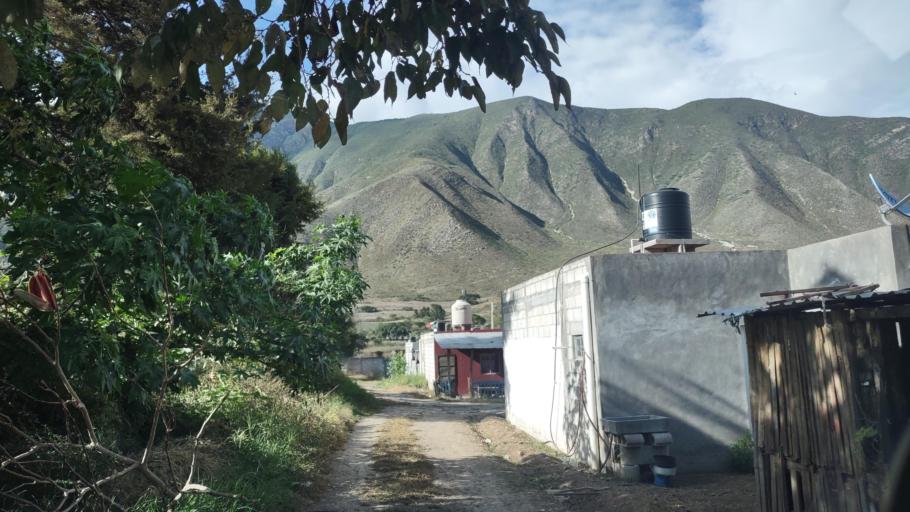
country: MX
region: Veracruz
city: Acultzingo
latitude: 18.7215
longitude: -97.3063
